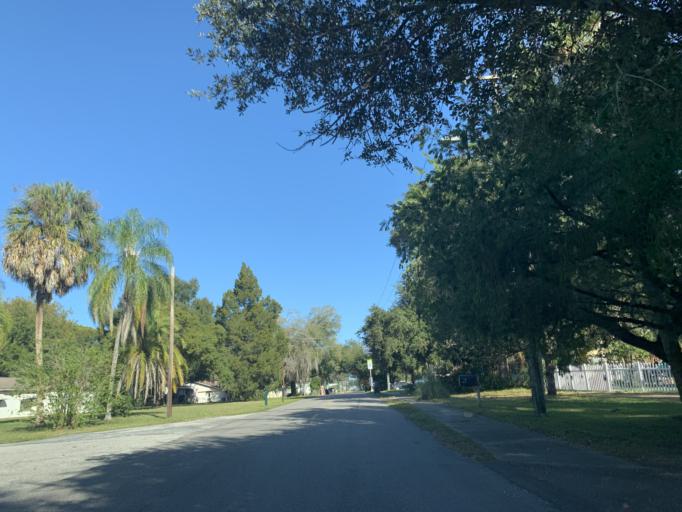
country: US
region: Florida
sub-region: Hillsborough County
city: Temple Terrace
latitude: 28.0234
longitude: -82.4099
